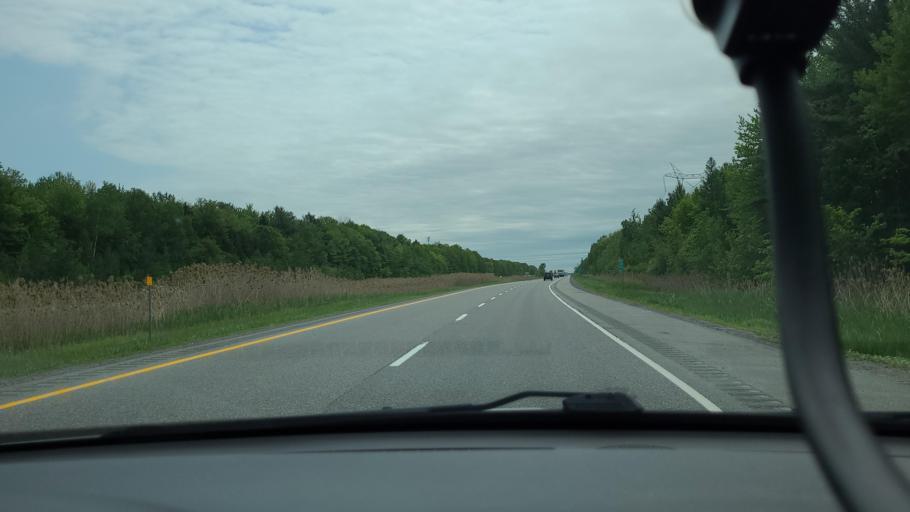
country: CA
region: Quebec
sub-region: Lanaudiere
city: Mascouche
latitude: 45.8123
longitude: -73.5947
